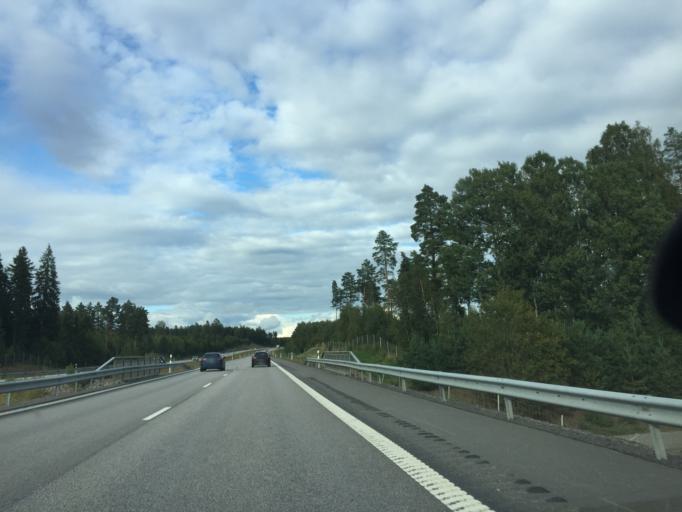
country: SE
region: OErebro
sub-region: Lindesbergs Kommun
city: Fellingsbro
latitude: 59.3613
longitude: 15.5712
